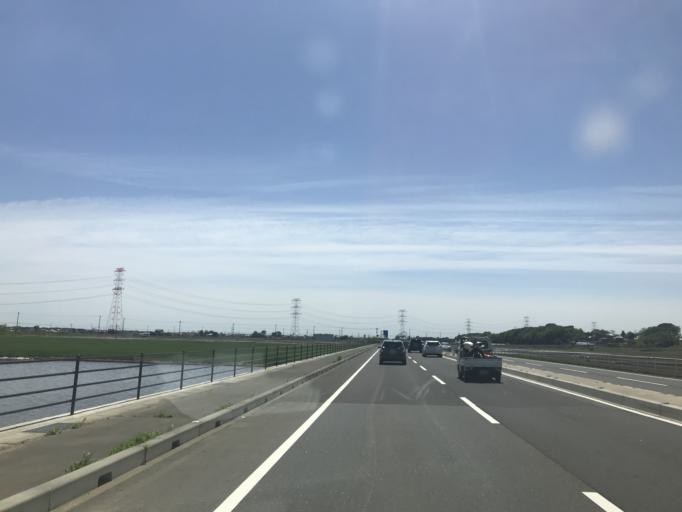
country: JP
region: Ibaraki
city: Shimodate
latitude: 36.2553
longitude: 139.9827
